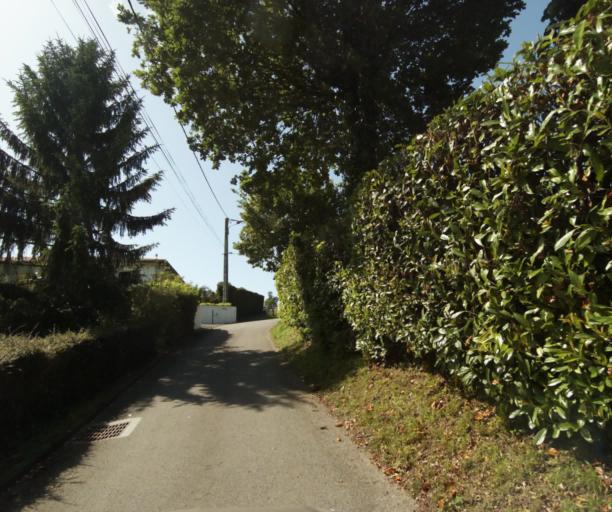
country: FR
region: Aquitaine
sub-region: Departement des Pyrenees-Atlantiques
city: Villefranque
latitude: 43.4595
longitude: -1.4446
